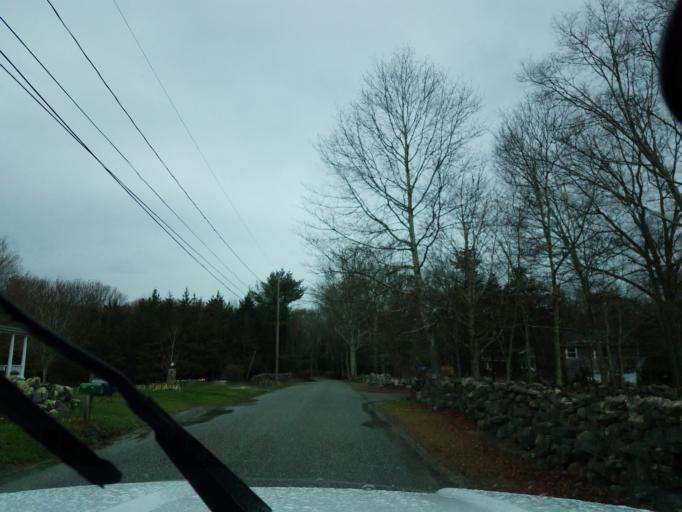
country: US
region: Rhode Island
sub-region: Washington County
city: Ashaway
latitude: 41.4484
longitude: -71.8226
